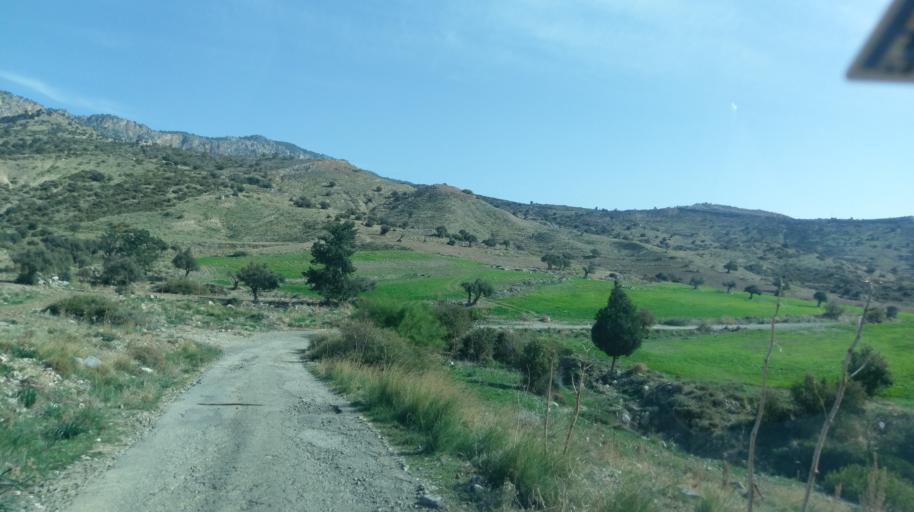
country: CY
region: Lefkosia
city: Nicosia
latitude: 35.2684
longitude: 33.3971
